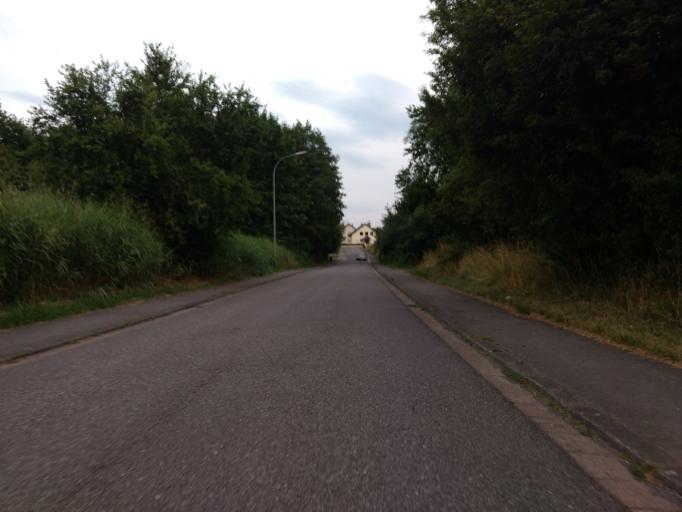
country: DE
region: Saarland
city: Wallerfangen
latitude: 49.3271
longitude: 6.7037
